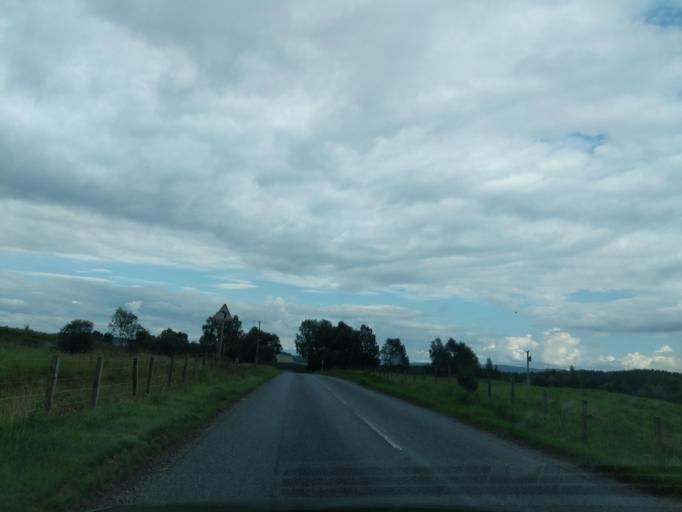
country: GB
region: Scotland
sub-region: Highland
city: Aviemore
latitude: 57.3027
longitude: -3.7506
